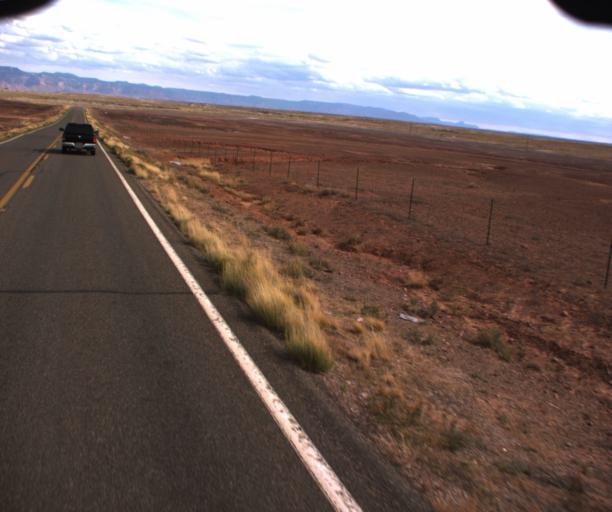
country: US
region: Arizona
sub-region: Apache County
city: Many Farms
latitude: 36.4692
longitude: -109.5338
